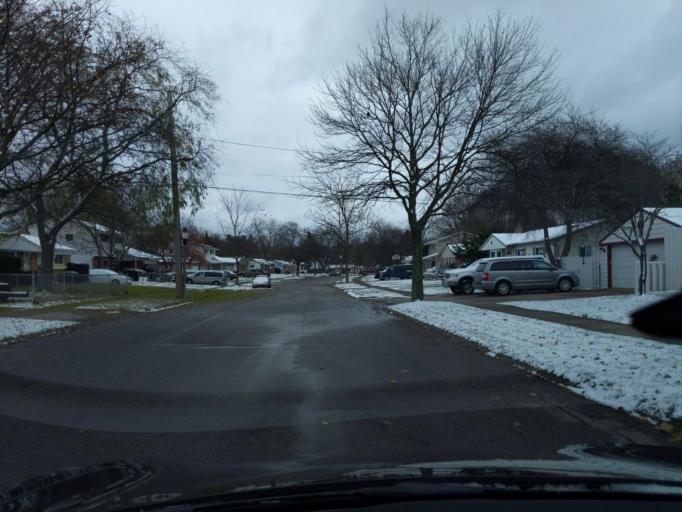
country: US
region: Michigan
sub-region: Eaton County
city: Waverly
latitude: 42.6856
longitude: -84.5956
